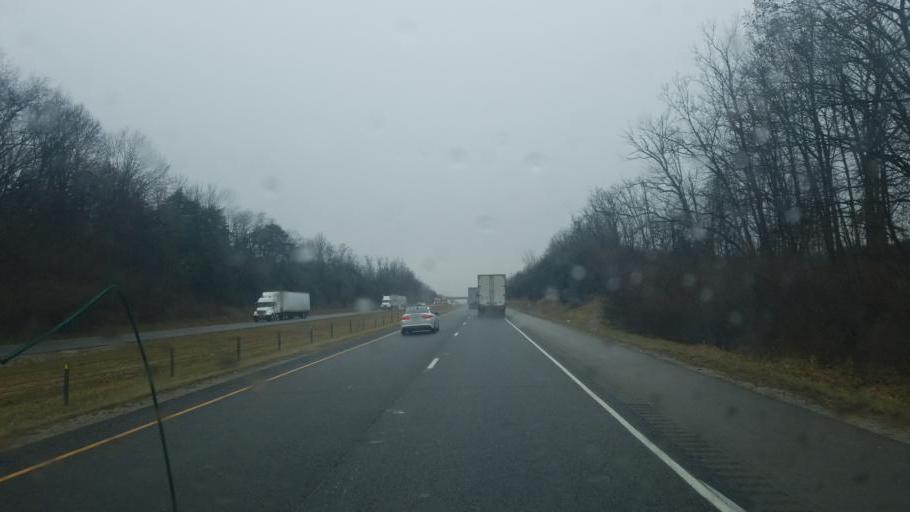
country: US
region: Ohio
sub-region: Preble County
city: New Paris
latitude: 39.8521
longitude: -84.8367
